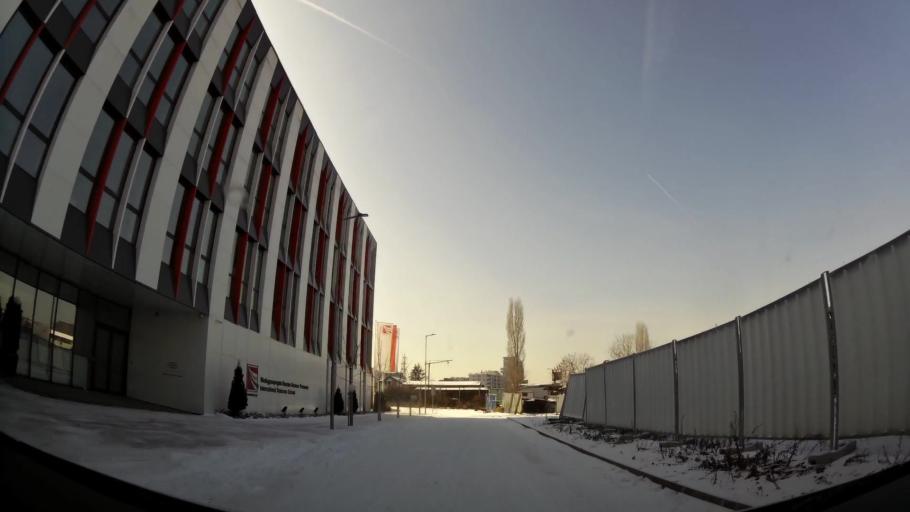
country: BG
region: Sofia-Capital
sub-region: Stolichna Obshtina
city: Sofia
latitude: 42.6561
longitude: 23.3178
